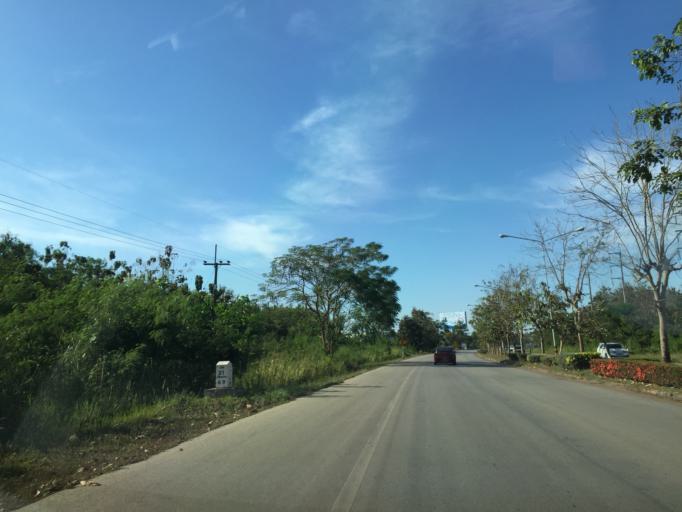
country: TH
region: Loei
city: Wang Saphung
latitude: 17.3202
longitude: 101.7639
